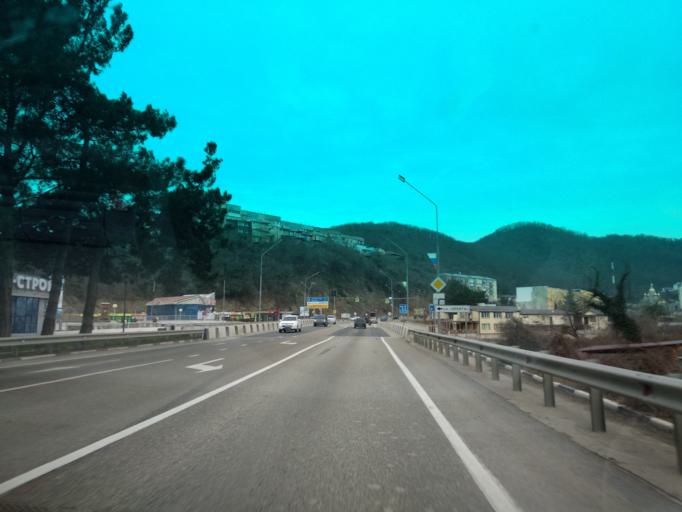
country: RU
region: Krasnodarskiy
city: Ol'ginka
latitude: 44.1986
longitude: 38.8894
